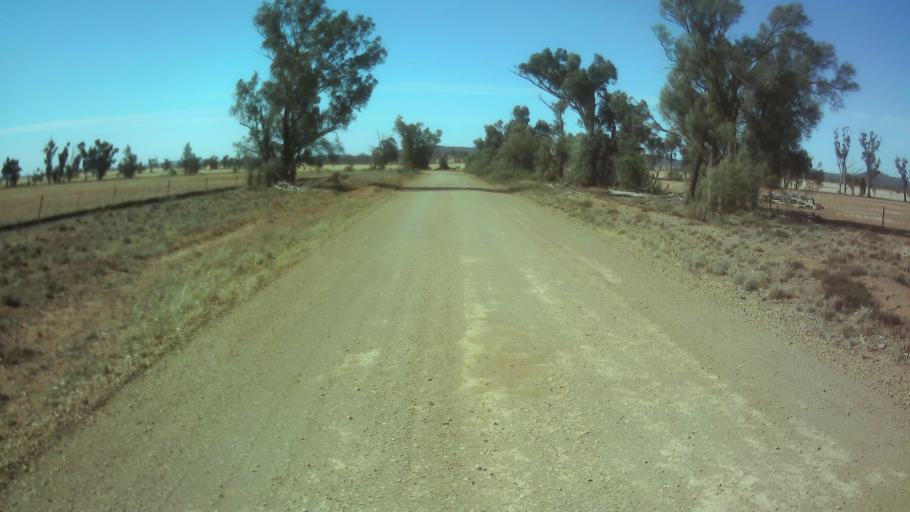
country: AU
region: New South Wales
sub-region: Forbes
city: Forbes
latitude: -33.7072
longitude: 147.7469
